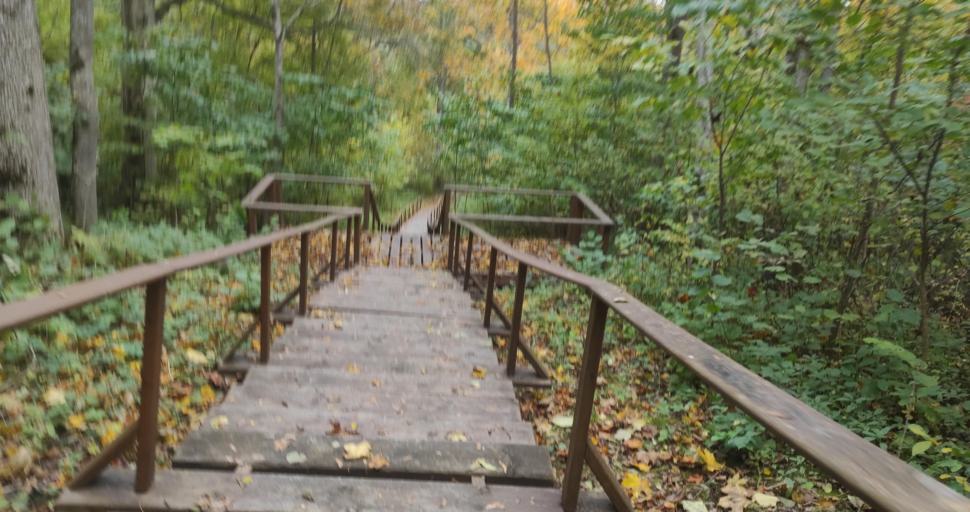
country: LV
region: Kandava
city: Kandava
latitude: 57.0153
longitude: 22.7582
